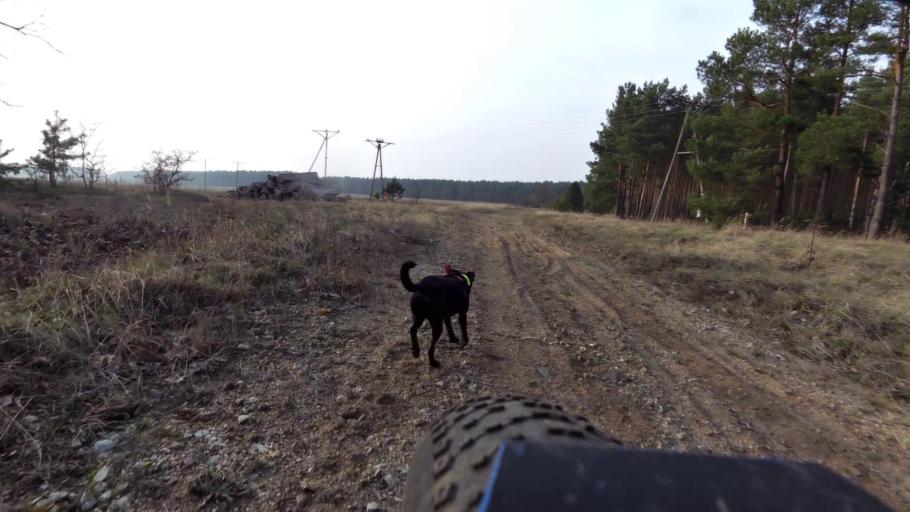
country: DE
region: Brandenburg
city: Vogelsang
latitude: 52.2592
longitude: 14.6929
